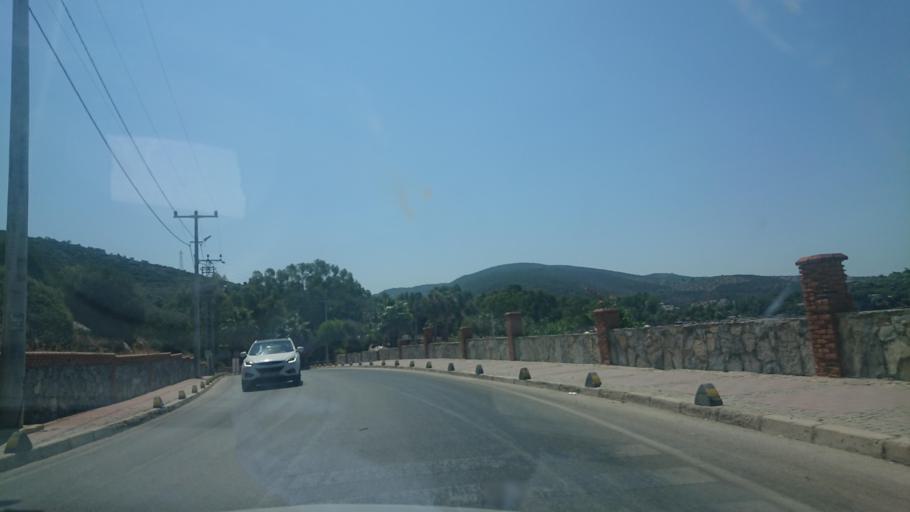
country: TR
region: Aydin
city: Kusadasi
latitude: 37.9042
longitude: 27.2717
